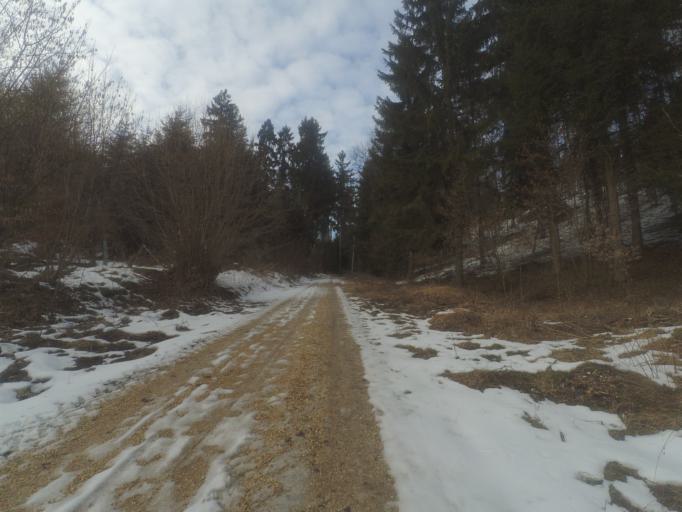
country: DE
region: Baden-Wuerttemberg
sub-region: Regierungsbezirk Stuttgart
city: Aalen
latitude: 48.8087
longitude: 10.0853
